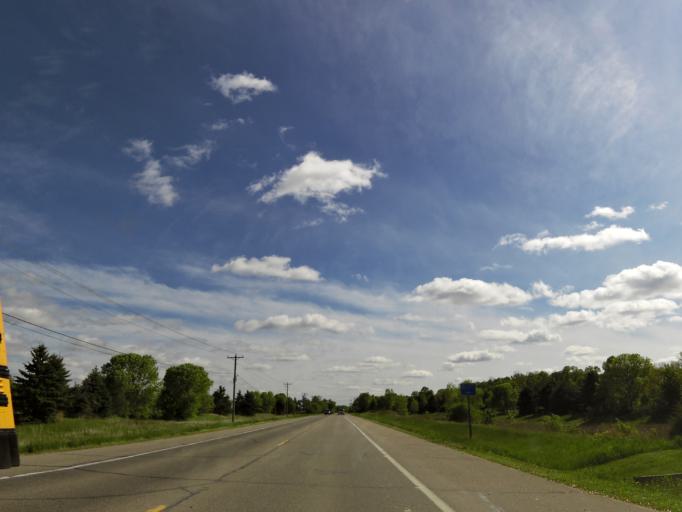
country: US
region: Wisconsin
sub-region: Saint Croix County
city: Hudson
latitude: 44.9832
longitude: -92.7907
